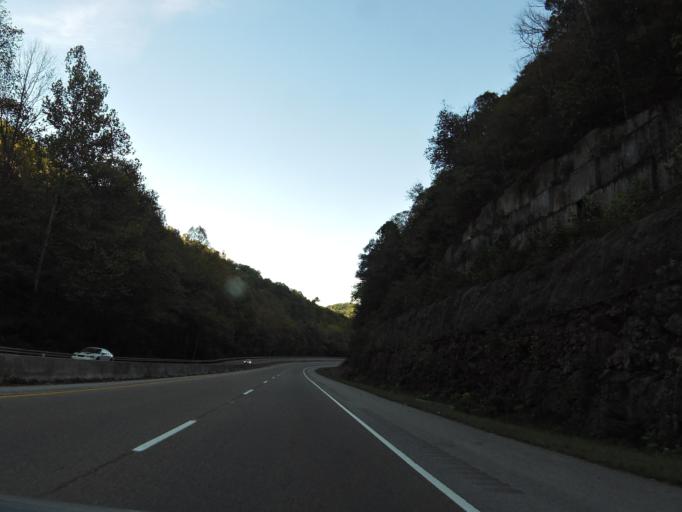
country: US
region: Tennessee
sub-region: Blount County
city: Wildwood
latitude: 35.7342
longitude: -83.8197
